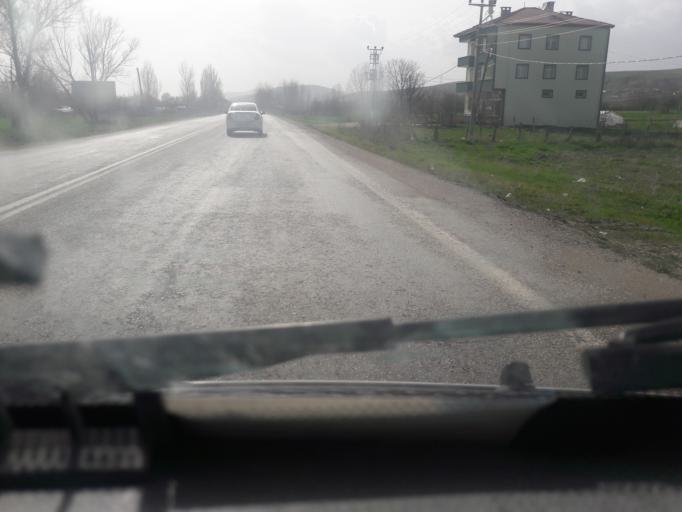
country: TR
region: Gumushane
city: Kelkit
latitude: 40.1429
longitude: 39.4295
